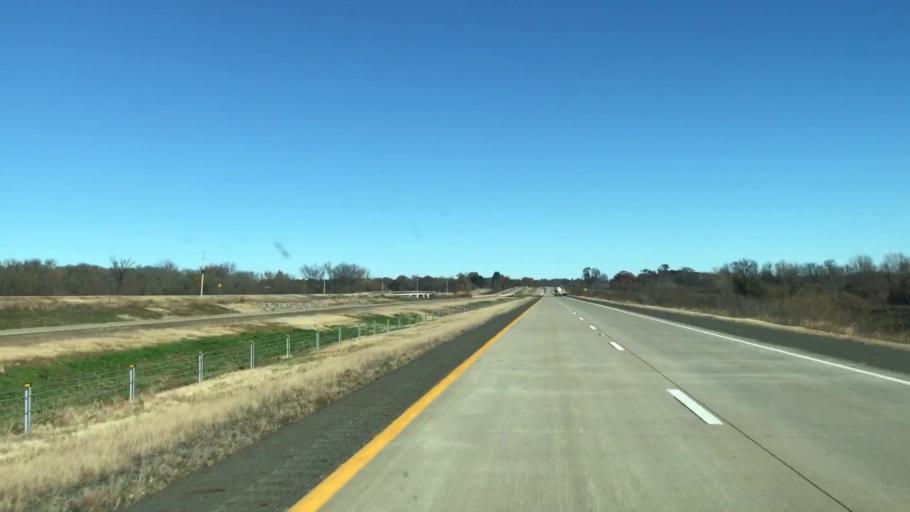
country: US
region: Texas
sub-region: Cass County
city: Queen City
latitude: 33.1446
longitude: -93.8922
